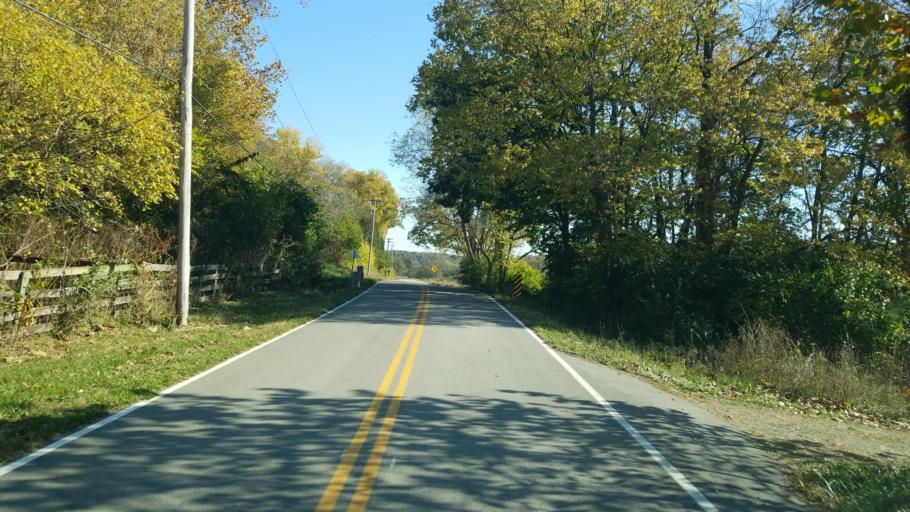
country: US
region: Ohio
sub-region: Warren County
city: Morrow
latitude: 39.3667
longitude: -84.1085
